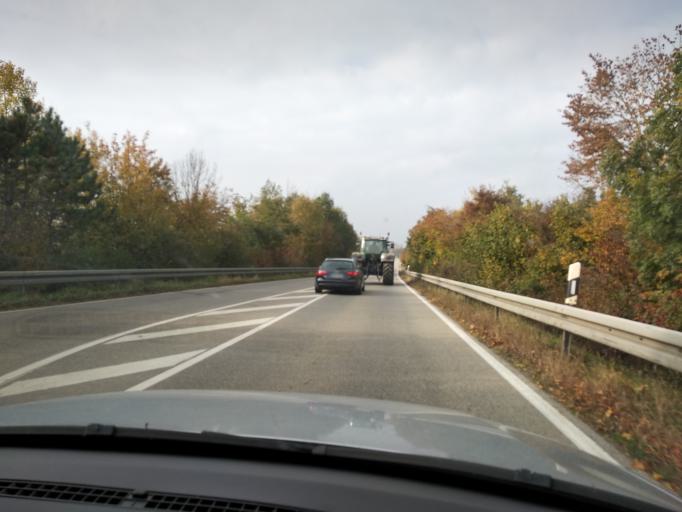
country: DE
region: Bavaria
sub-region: Upper Bavaria
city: Forstinning
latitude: 48.1713
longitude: 11.8894
